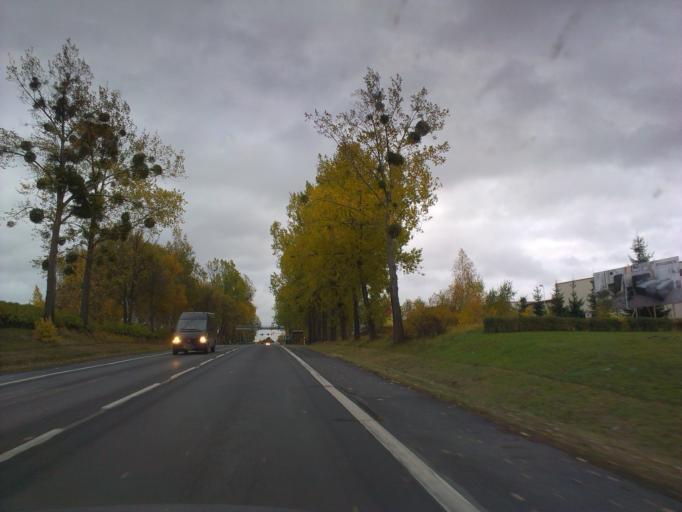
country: PL
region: Kujawsko-Pomorskie
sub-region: Powiat chelminski
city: Chelmno
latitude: 53.3461
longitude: 18.4543
